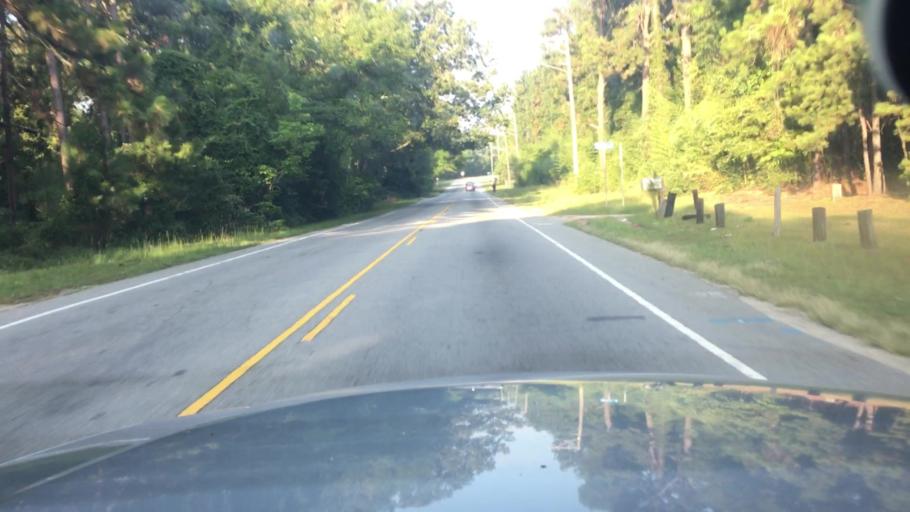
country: US
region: North Carolina
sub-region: Cumberland County
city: Spring Lake
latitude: 35.1059
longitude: -78.9461
